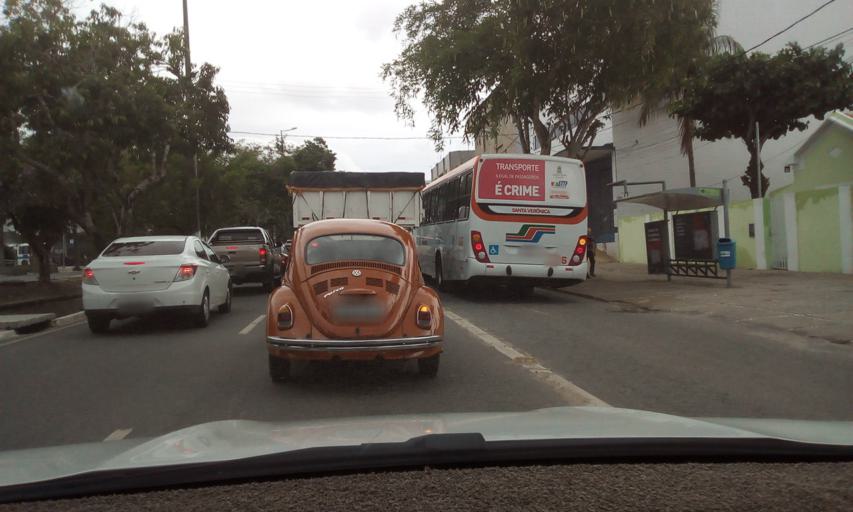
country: BR
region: Paraiba
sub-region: Campina Grande
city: Campina Grande
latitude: -7.2188
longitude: -35.8755
